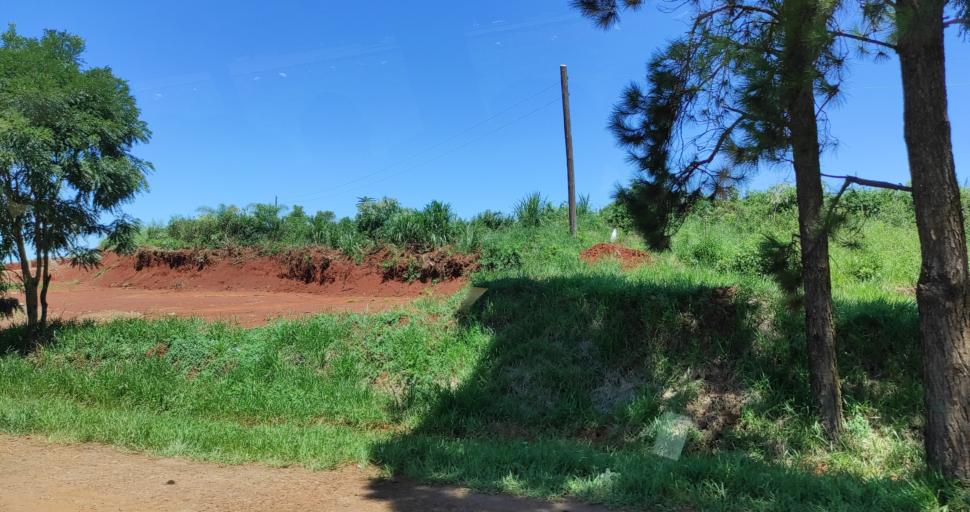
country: AR
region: Misiones
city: Dos de Mayo
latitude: -27.0114
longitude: -54.4695
